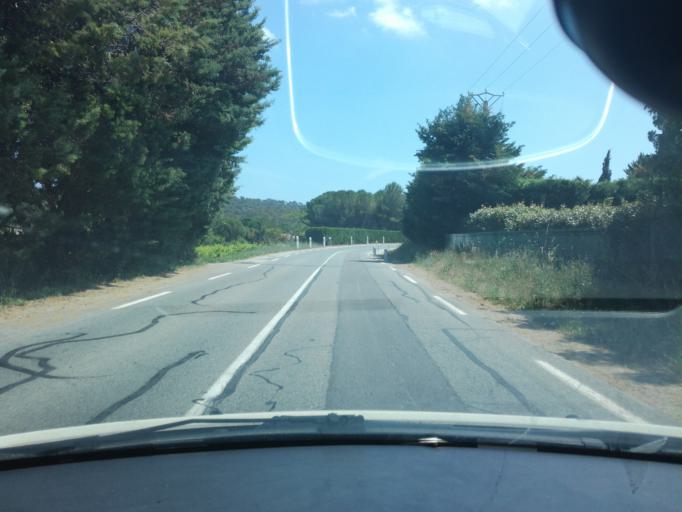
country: FR
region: Provence-Alpes-Cote d'Azur
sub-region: Departement du Var
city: Le Muy
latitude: 43.4870
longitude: 6.5667
